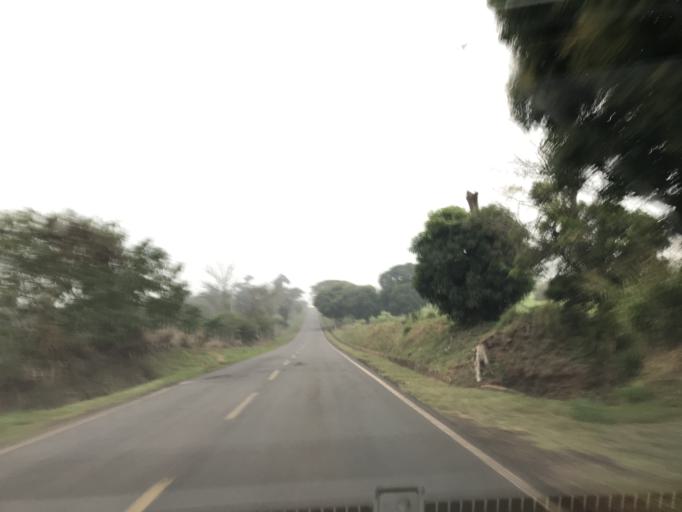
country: PY
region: Canindeyu
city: Salto del Guaira
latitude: -24.0937
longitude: -54.0965
